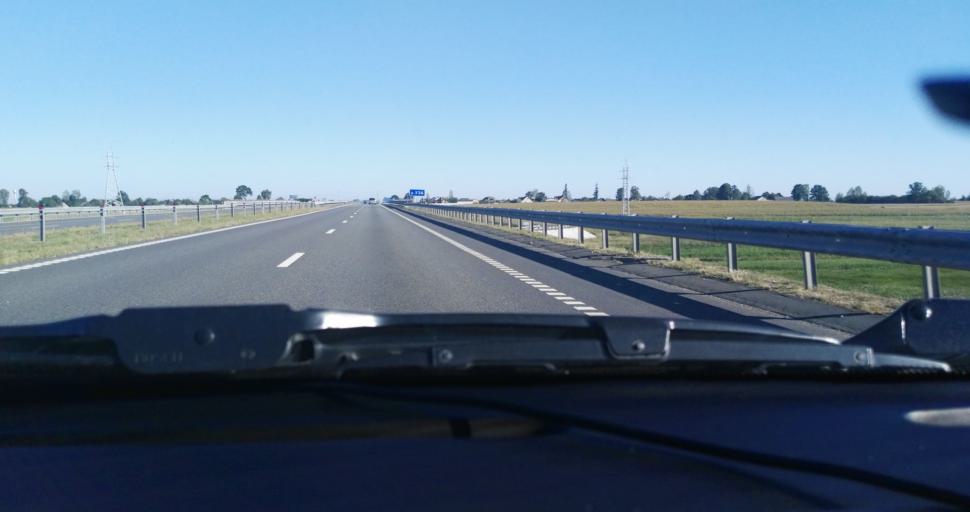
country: BY
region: Gomel
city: Buda-Kashalyova
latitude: 52.5129
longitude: 30.6299
